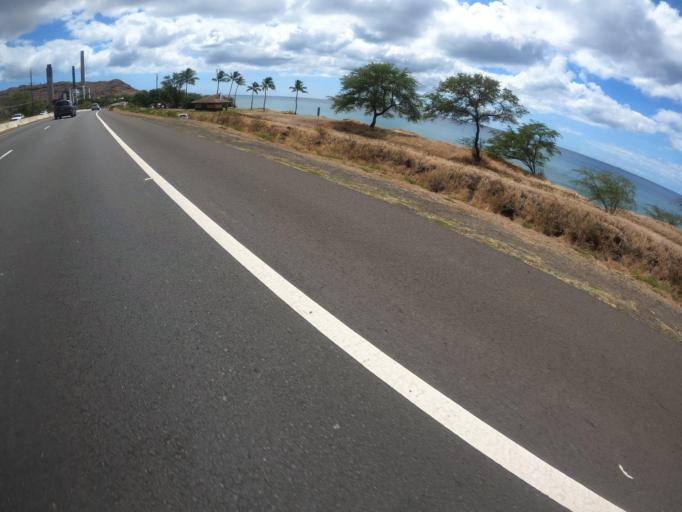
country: US
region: Hawaii
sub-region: Honolulu County
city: Nanakuli
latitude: 21.3623
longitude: -158.1324
